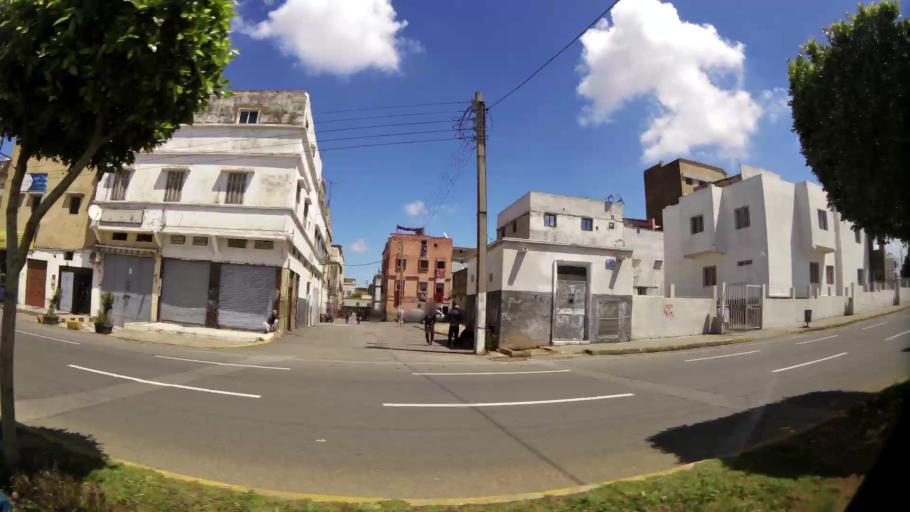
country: MA
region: Grand Casablanca
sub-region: Casablanca
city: Casablanca
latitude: 33.5605
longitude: -7.5757
